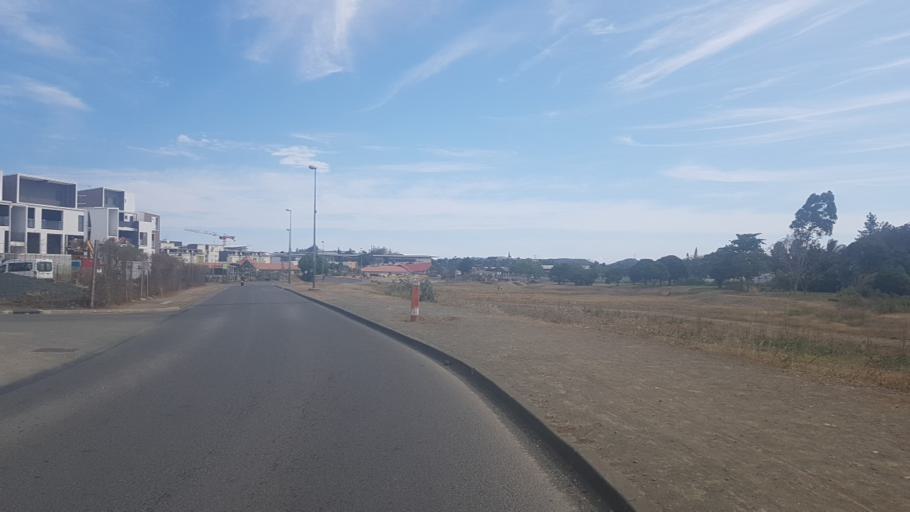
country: NC
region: South Province
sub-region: Noumea
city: Noumea
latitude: -22.2131
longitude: 166.4747
